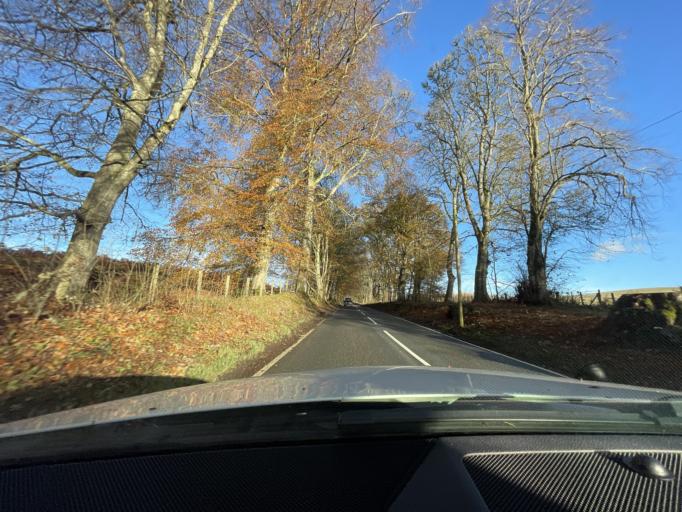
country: GB
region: Scotland
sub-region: Highland
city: Inverness
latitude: 57.4310
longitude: -4.2785
